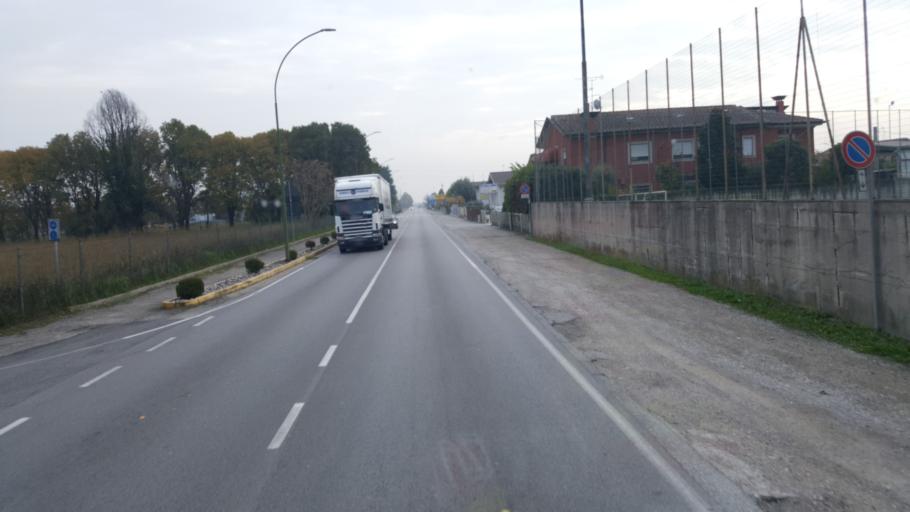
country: IT
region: Lombardy
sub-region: Provincia di Mantova
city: Guidizzolo
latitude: 45.3179
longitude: 10.5853
